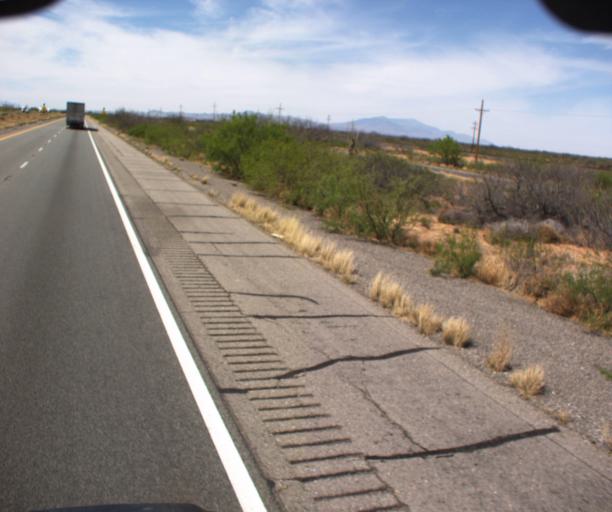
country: US
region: Arizona
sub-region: Cochise County
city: Willcox
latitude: 32.3122
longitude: -109.4184
